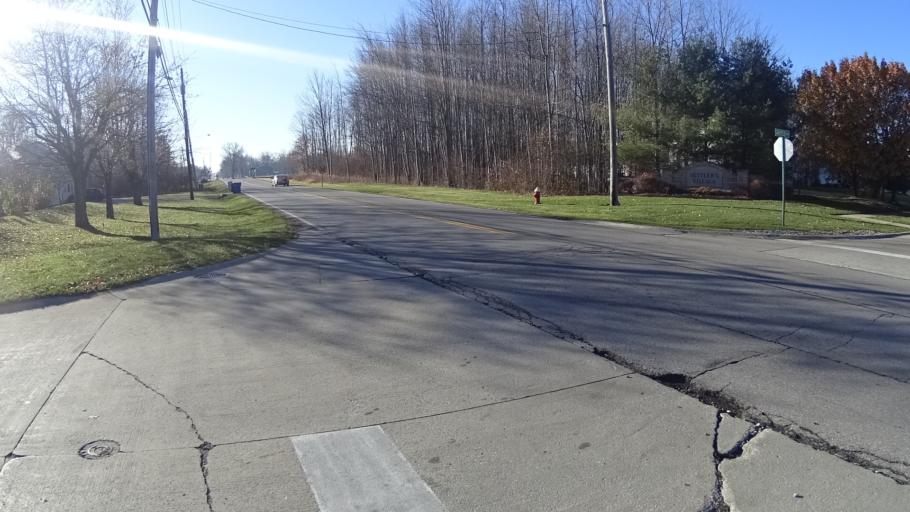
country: US
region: Ohio
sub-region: Lorain County
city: Sheffield Lake
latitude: 41.4567
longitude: -82.0763
